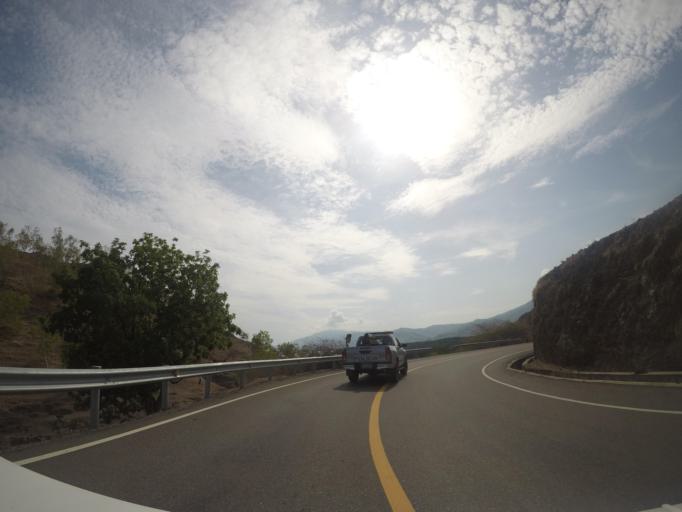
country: ID
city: Metinaro
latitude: -8.5217
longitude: 125.7172
